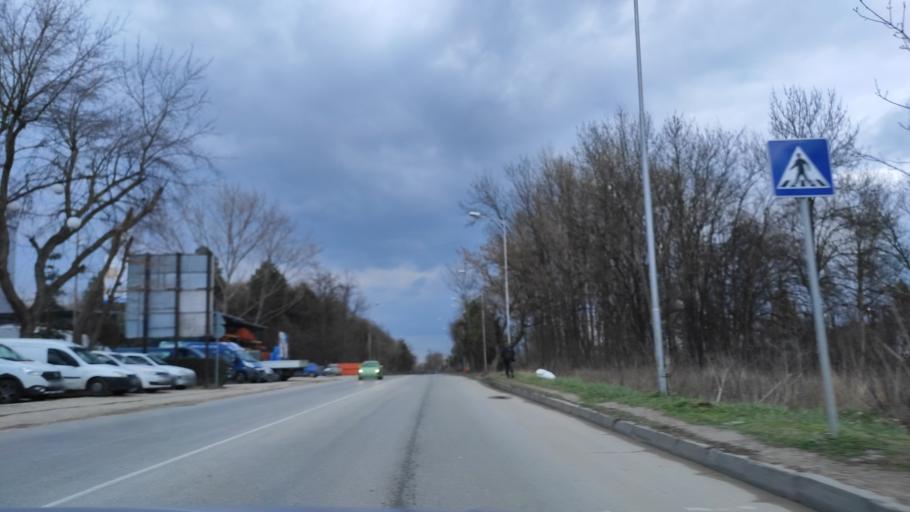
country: BG
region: Varna
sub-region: Obshtina Aksakovo
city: Aksakovo
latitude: 43.2249
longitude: 27.8617
